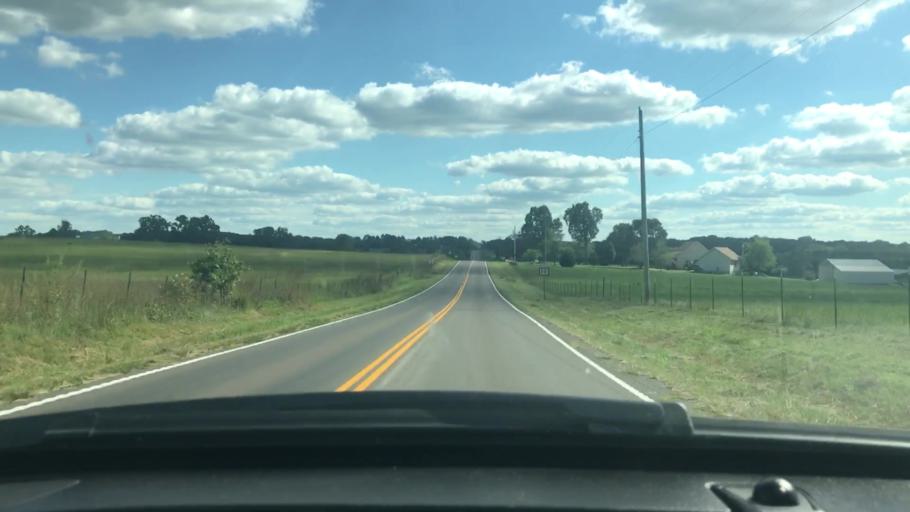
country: US
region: Missouri
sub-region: Wright County
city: Mountain Grove
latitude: 37.2452
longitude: -92.3001
